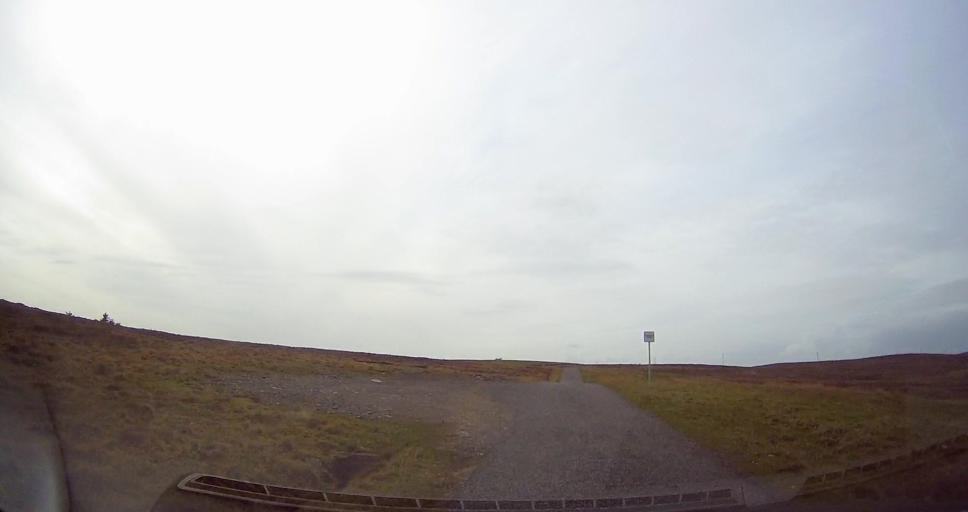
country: GB
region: Scotland
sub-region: Shetland Islands
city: Shetland
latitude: 60.1523
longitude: -1.0903
